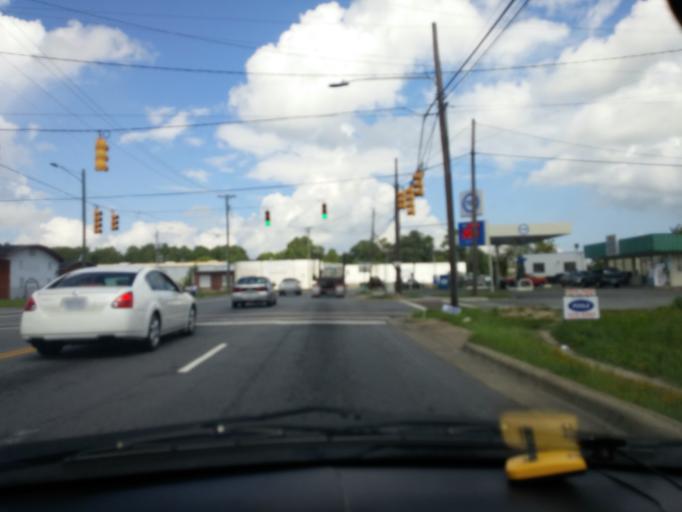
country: US
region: North Carolina
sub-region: Lenoir County
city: Kinston
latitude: 35.2683
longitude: -77.5719
